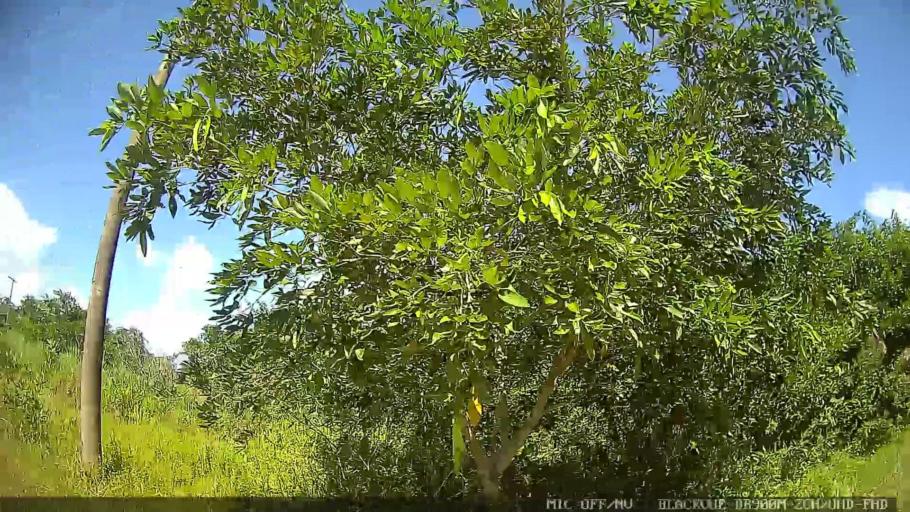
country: BR
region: Sao Paulo
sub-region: Itanhaem
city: Itanhaem
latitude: -24.2285
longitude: -46.8796
